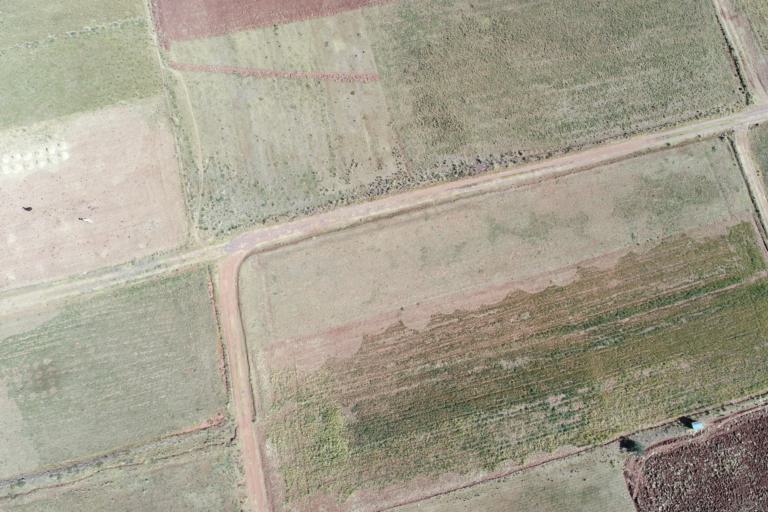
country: BO
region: La Paz
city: Tiahuanaco
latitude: -16.6023
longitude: -68.7813
